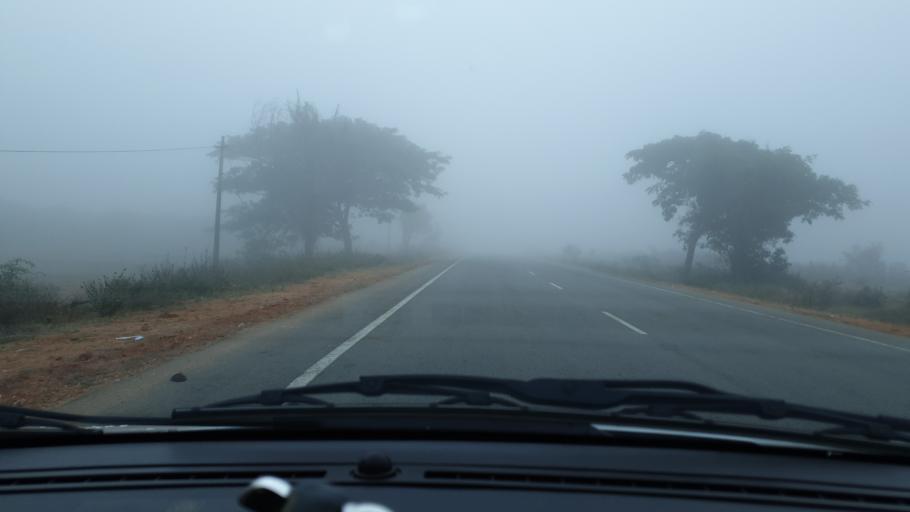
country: IN
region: Telangana
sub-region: Mahbubnagar
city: Nagar Karnul
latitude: 16.6853
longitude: 78.5239
